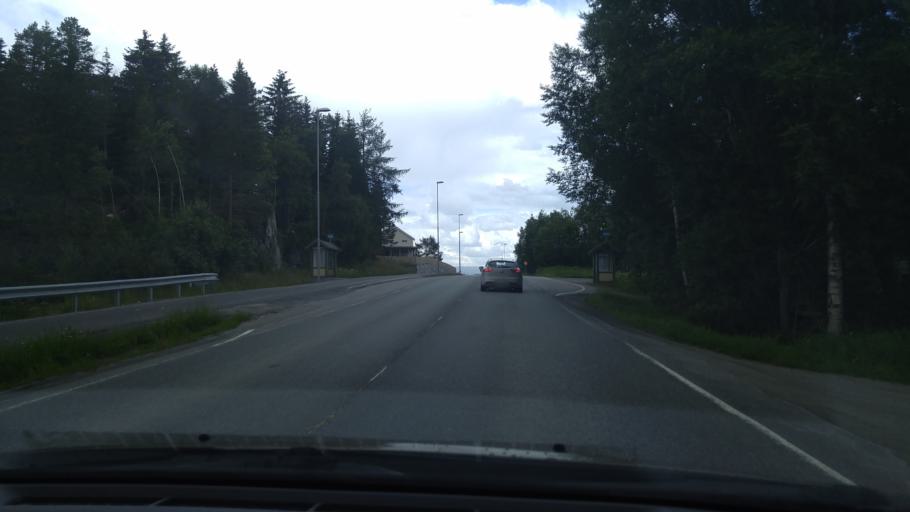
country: NO
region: Nord-Trondelag
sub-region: Namsos
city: Namsos
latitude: 64.4379
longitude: 11.5082
